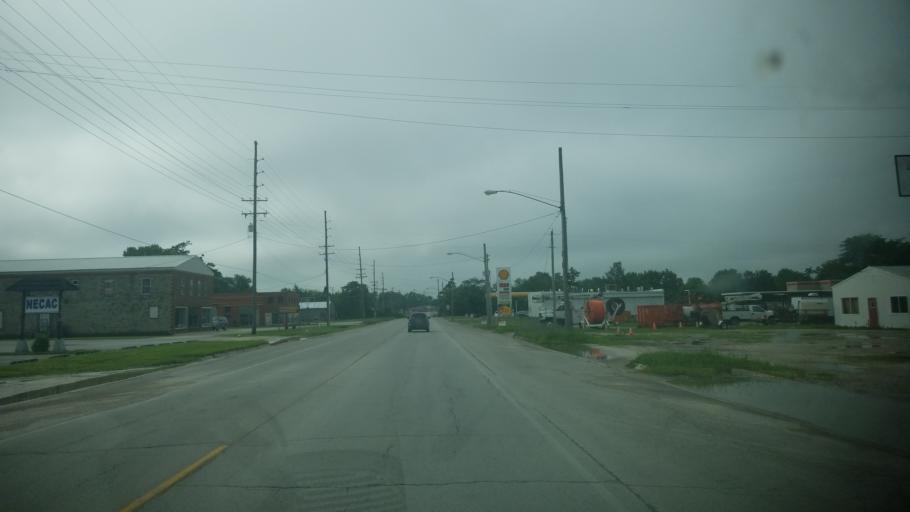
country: US
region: Missouri
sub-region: Pike County
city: Bowling Green
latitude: 39.3481
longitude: -91.2064
